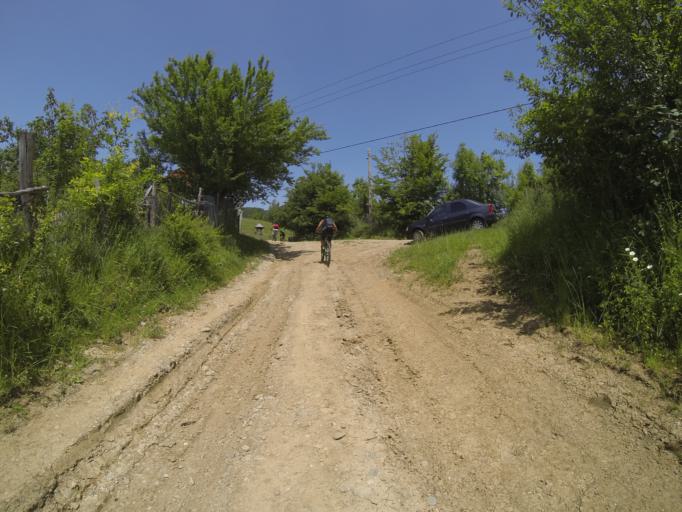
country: RO
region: Valcea
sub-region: Oras Baile Olanesti
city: Baile Olanesti
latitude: 45.2046
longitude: 24.2121
